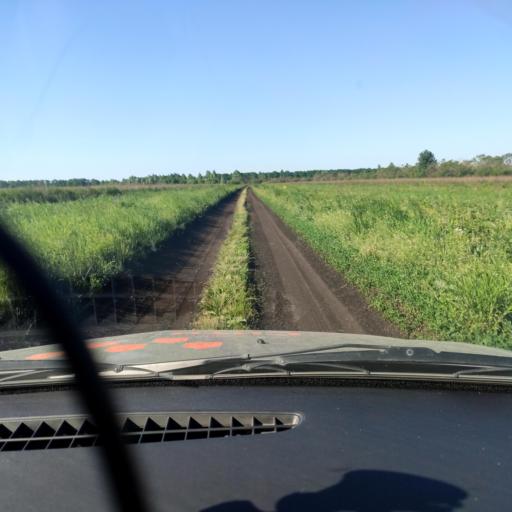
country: RU
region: Bashkortostan
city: Avdon
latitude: 54.5660
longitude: 55.8310
